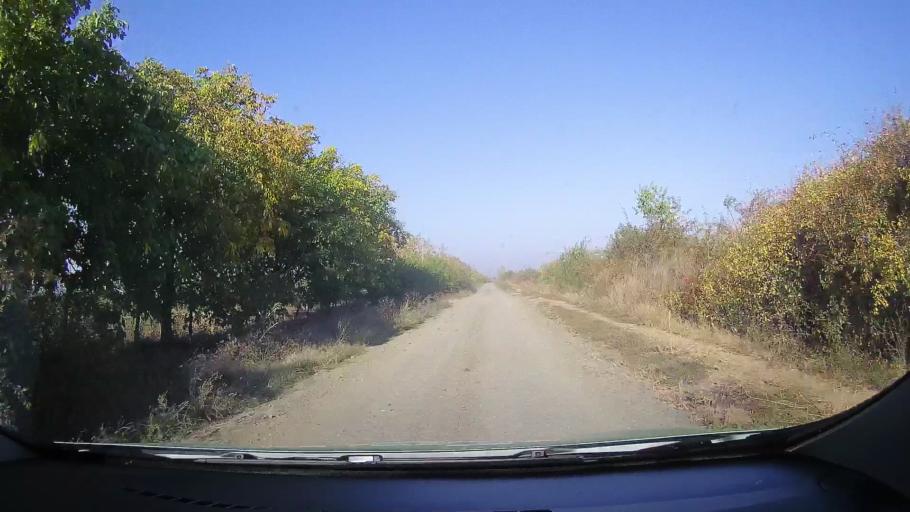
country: RO
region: Satu Mare
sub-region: Comuna Sauca
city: Sauca
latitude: 47.4738
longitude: 22.4813
